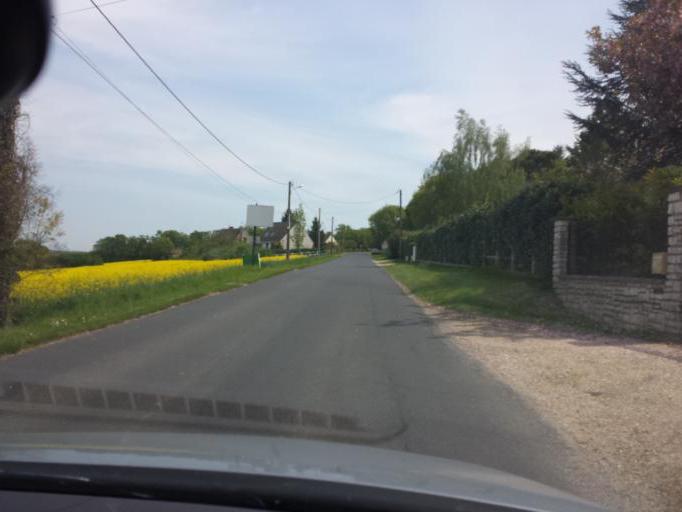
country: FR
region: Centre
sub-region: Departement d'Eure-et-Loir
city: Anet
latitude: 48.8525
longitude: 1.4483
